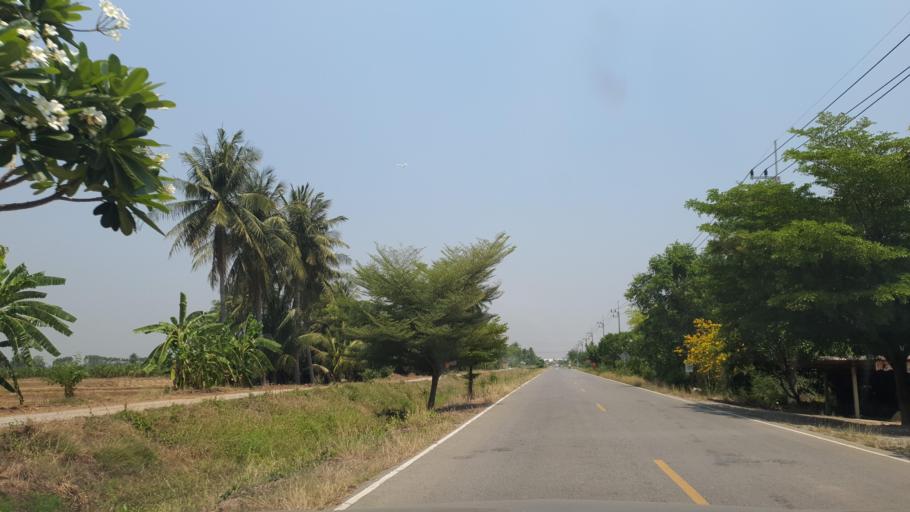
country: TH
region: Suphan Buri
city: Si Prachan
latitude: 14.5877
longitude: 100.1070
